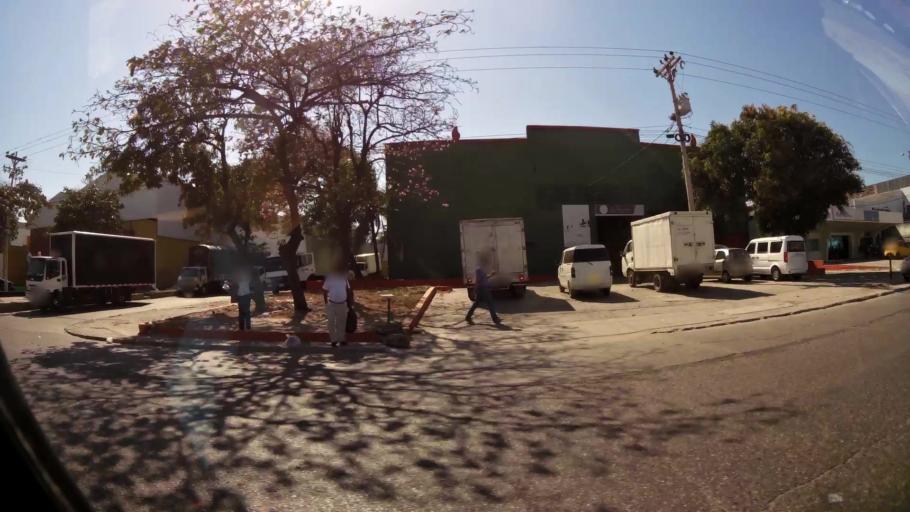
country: CO
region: Atlantico
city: Barranquilla
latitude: 10.9503
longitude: -74.7859
